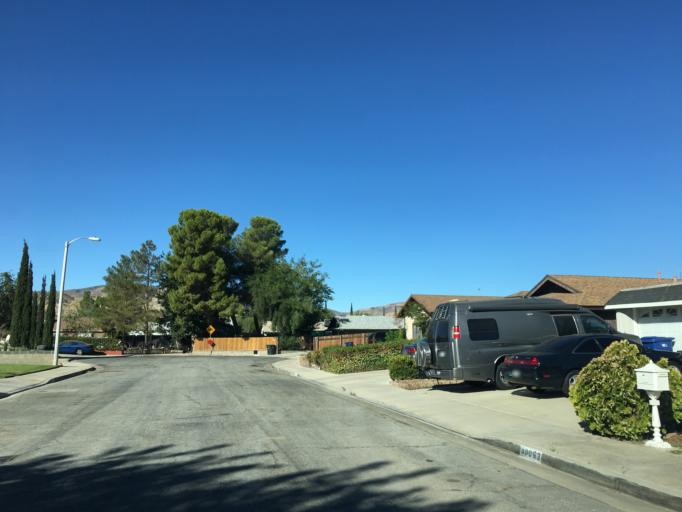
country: US
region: California
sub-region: Los Angeles County
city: Desert View Highlands
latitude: 34.5925
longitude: -118.1552
